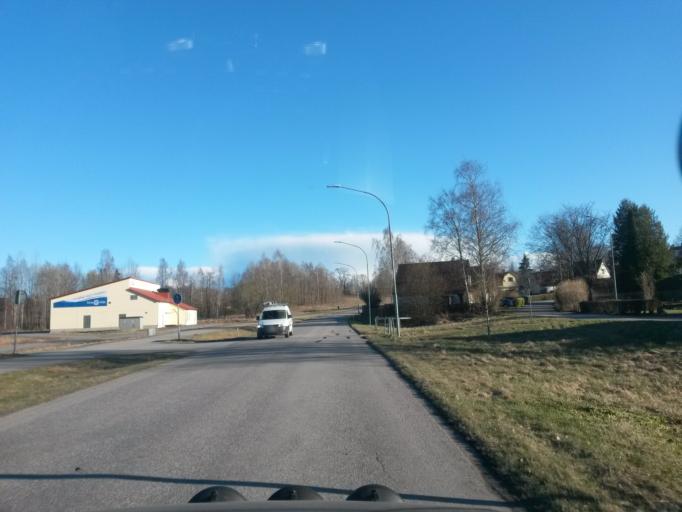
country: SE
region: OErebro
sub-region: Karlskoga Kommun
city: Karlskoga
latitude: 59.3135
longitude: 14.5137
